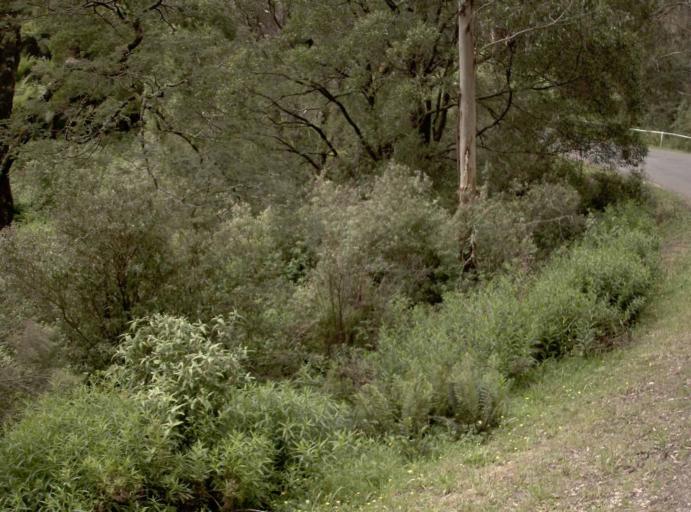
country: AU
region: Victoria
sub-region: Latrobe
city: Traralgon
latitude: -38.4263
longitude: 146.5673
